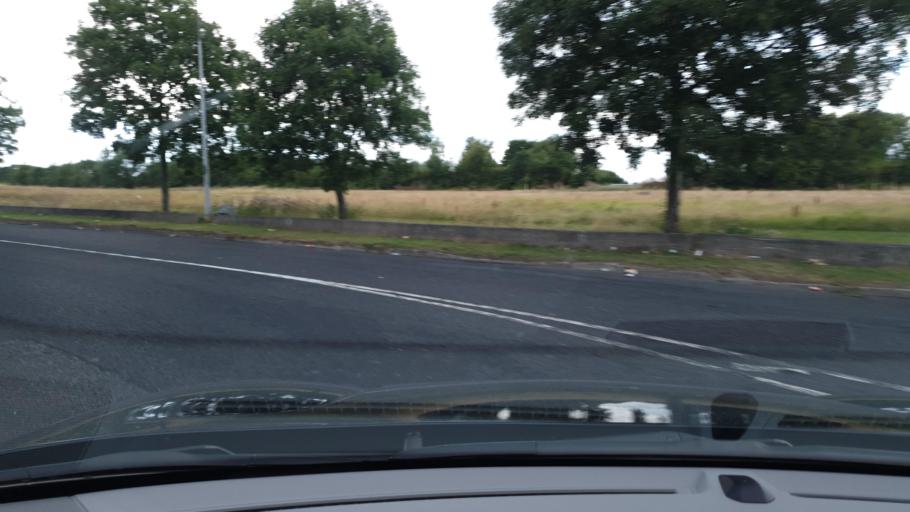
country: IE
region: Leinster
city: Clondalkin
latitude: 53.3284
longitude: -6.4112
